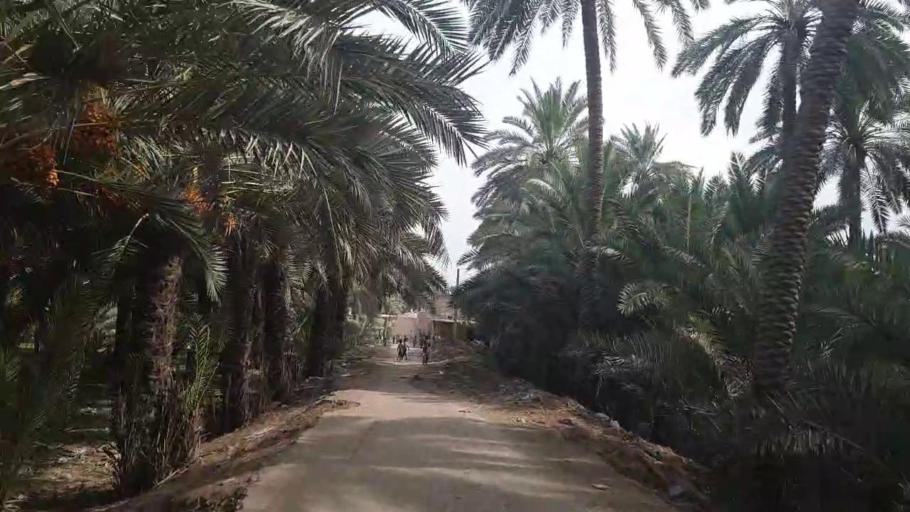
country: PK
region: Sindh
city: Sukkur
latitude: 27.6417
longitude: 68.8025
